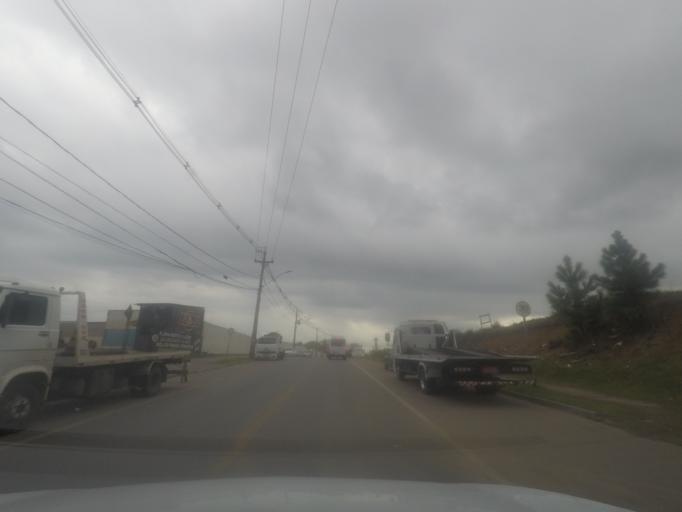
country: BR
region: Parana
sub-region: Sao Jose Dos Pinhais
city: Sao Jose dos Pinhais
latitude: -25.5609
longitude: -49.2647
